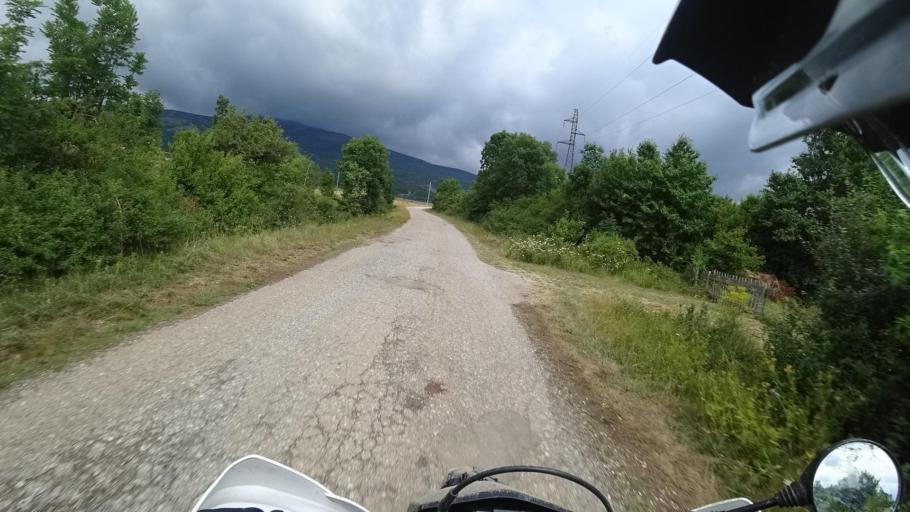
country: HR
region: Zadarska
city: Gracac
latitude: 44.5307
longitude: 15.8292
